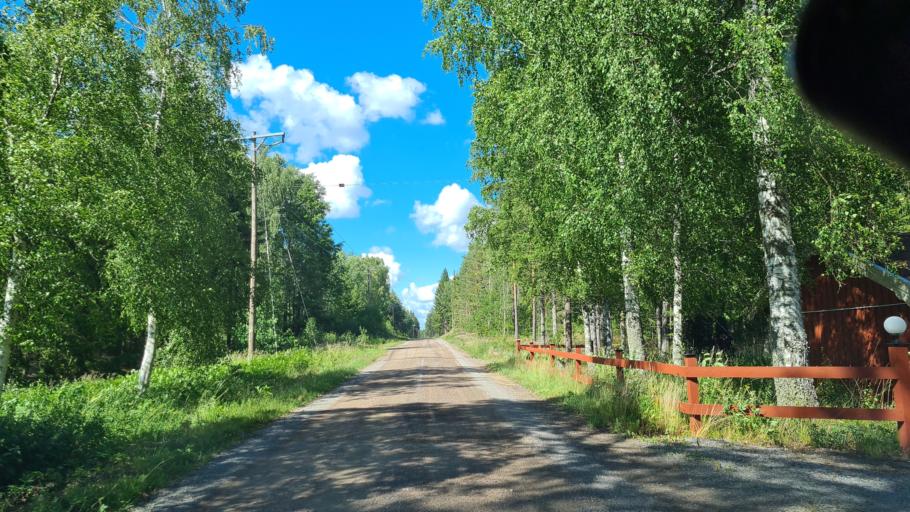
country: SE
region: OEstergoetland
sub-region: Norrkopings Kommun
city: Krokek
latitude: 58.6840
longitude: 16.4363
